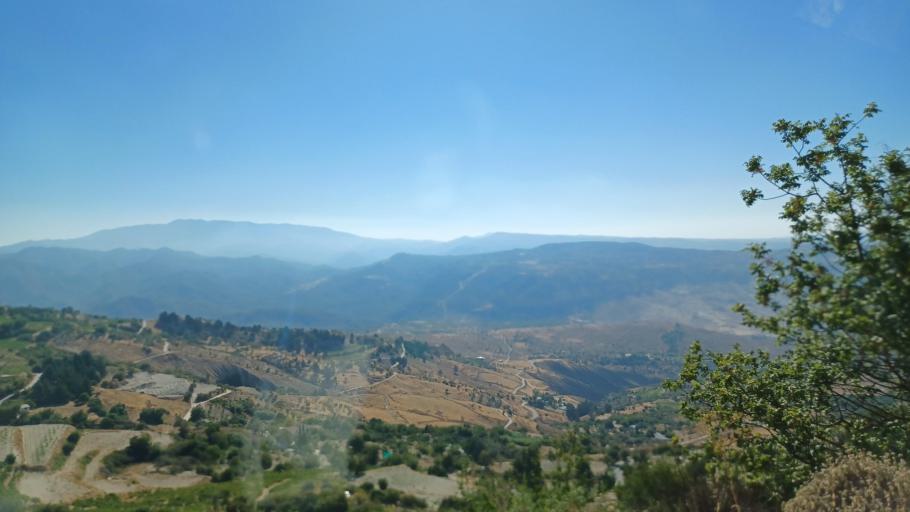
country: CY
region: Pafos
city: Mesogi
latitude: 34.8905
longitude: 32.6264
